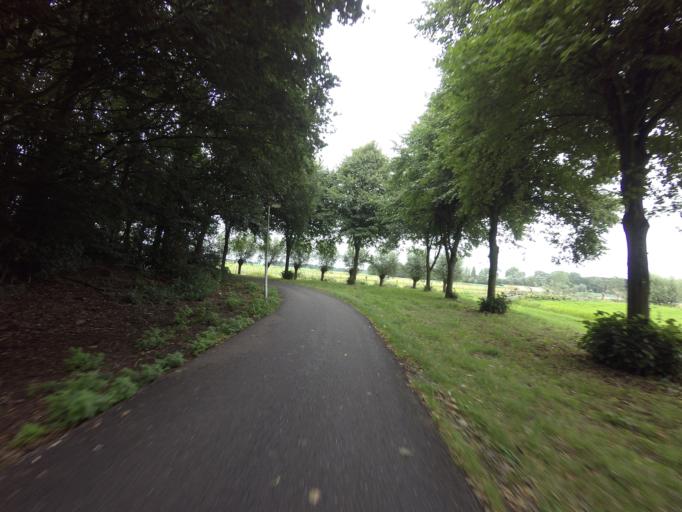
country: NL
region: South Holland
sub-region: Gemeente Teylingen
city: Voorhout
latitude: 52.2009
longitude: 4.4940
